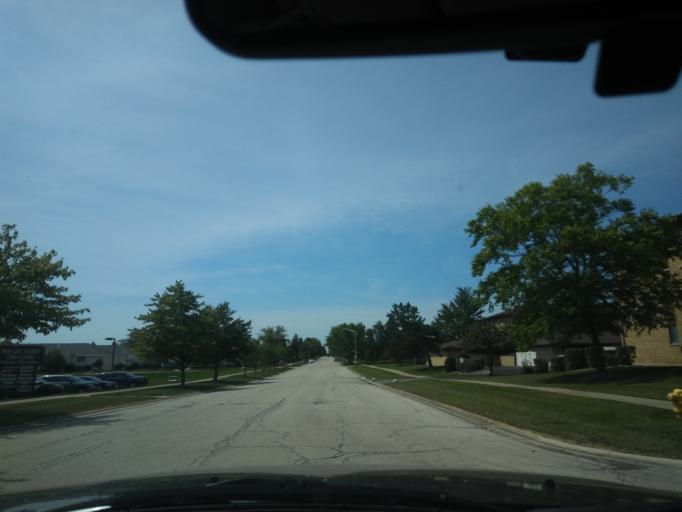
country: US
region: Illinois
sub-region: Cook County
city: Tinley Park
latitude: 41.6163
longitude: -87.7968
